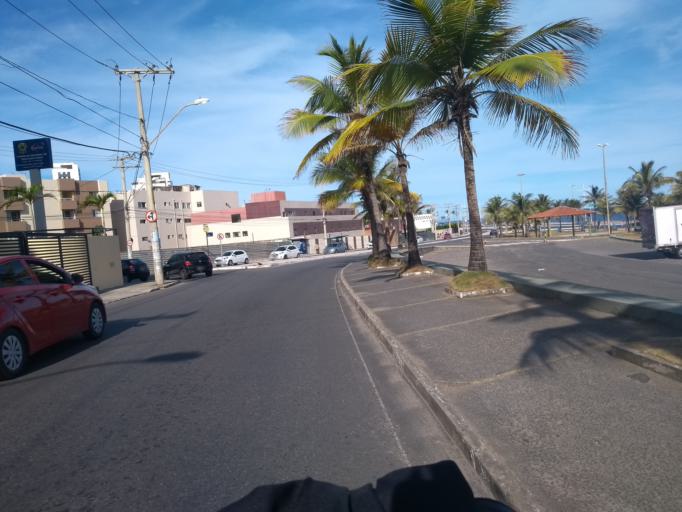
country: BR
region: Bahia
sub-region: Salvador
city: Salvador
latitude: -12.9973
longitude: -38.4468
